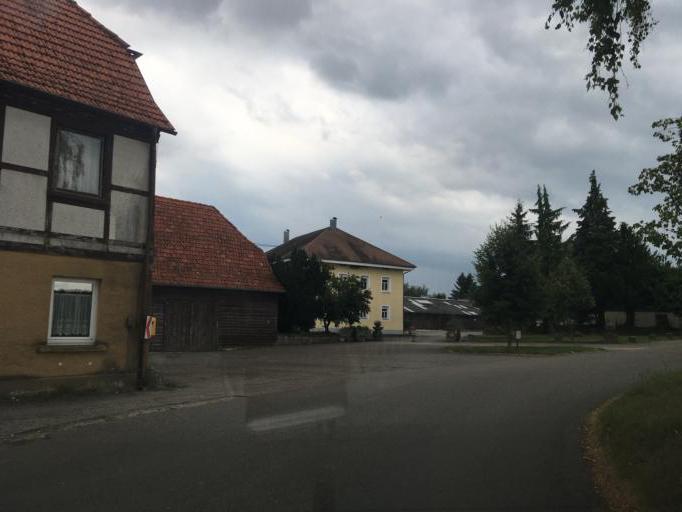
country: DE
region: Baden-Wuerttemberg
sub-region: Tuebingen Region
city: Kirchentellinsfurt
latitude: 48.5561
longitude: 9.1350
